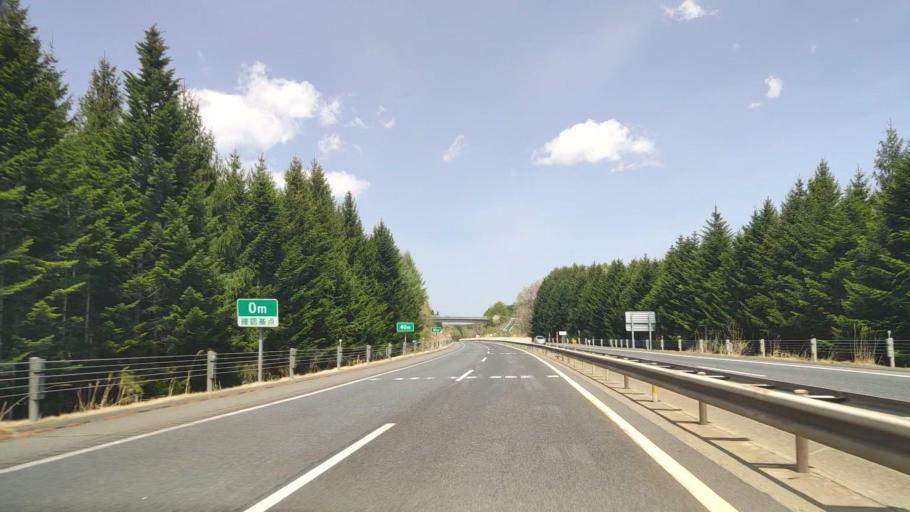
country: JP
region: Aomori
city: Hachinohe
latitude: 40.4131
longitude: 141.4433
